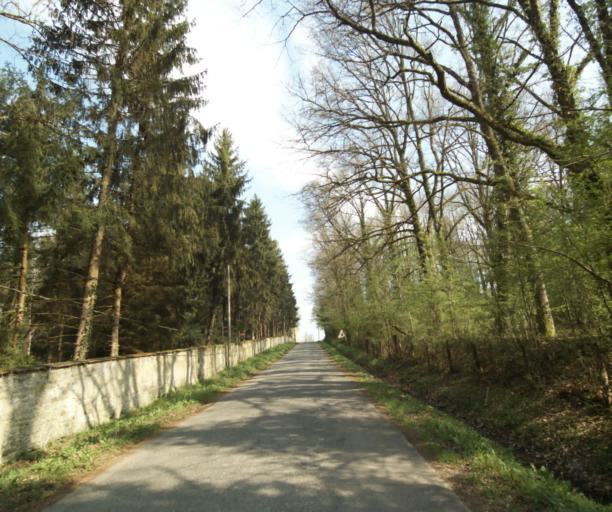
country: FR
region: Bourgogne
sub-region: Departement de Saone-et-Loire
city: Palinges
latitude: 46.5195
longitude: 4.2110
